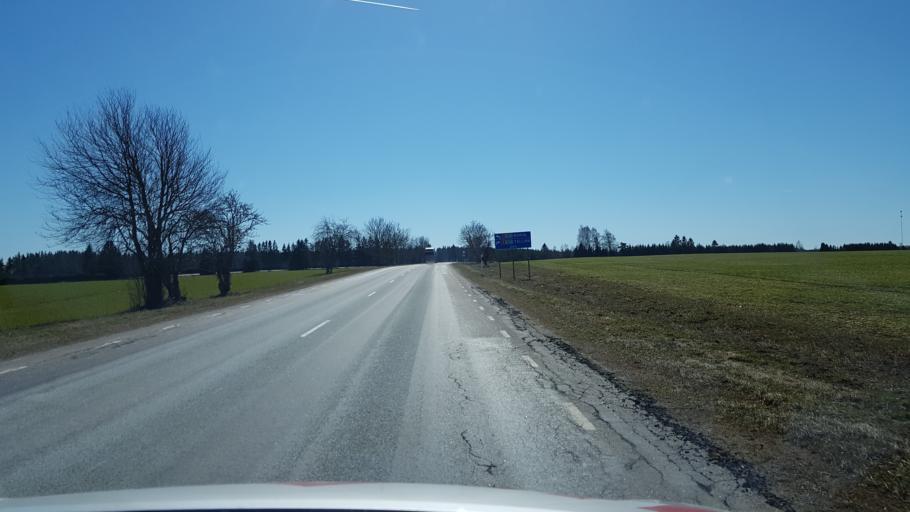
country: EE
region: Ida-Virumaa
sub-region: Aseri vald
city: Aseri
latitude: 59.4334
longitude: 26.6984
